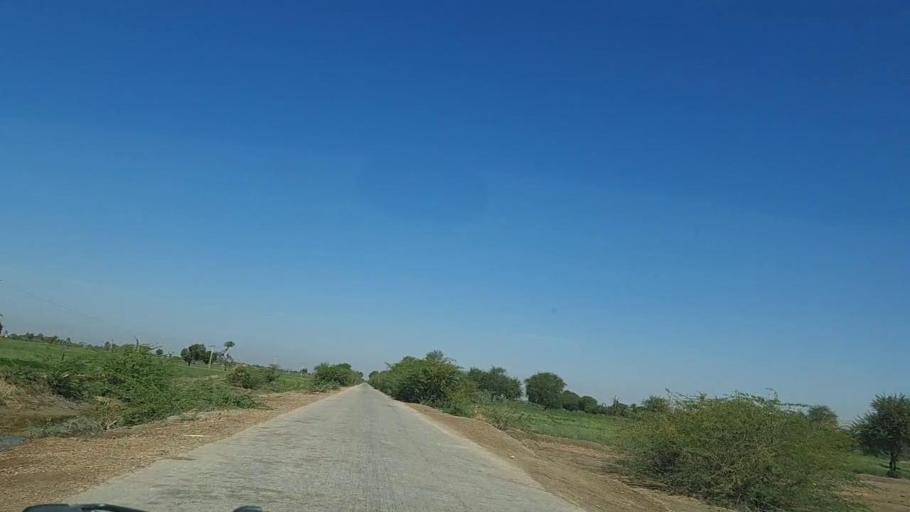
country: PK
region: Sindh
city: Dhoro Naro
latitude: 25.4655
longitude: 69.5261
